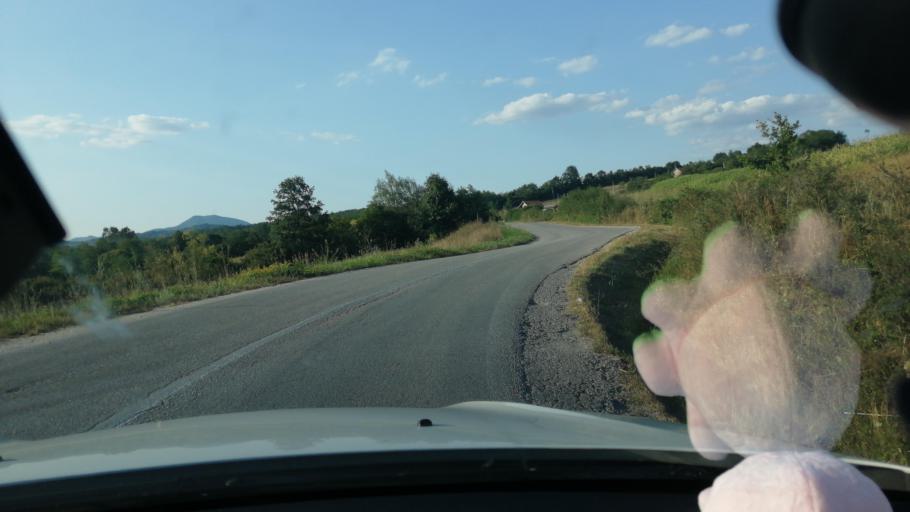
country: RS
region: Central Serbia
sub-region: Moravicki Okrug
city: Lucani
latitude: 43.8024
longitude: 20.2537
